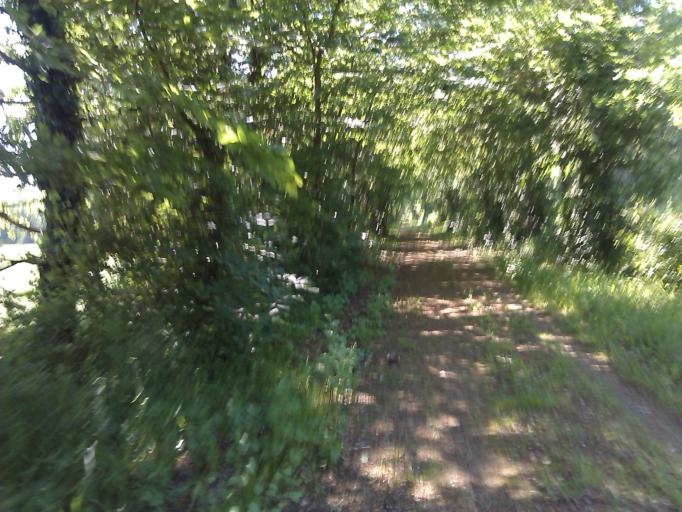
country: FR
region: Centre
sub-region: Departement de l'Indre
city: Saint-Gaultier
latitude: 46.6442
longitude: 1.3246
